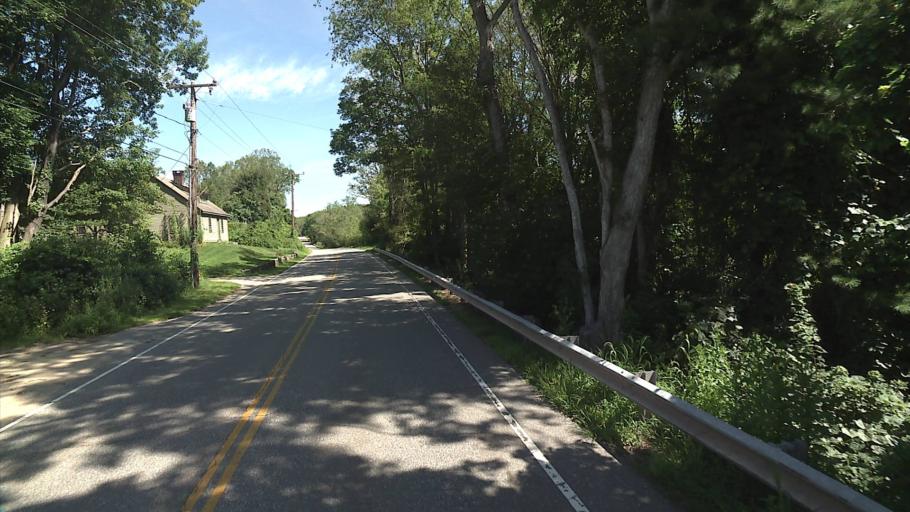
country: US
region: Connecticut
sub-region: New London County
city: Baltic
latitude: 41.6740
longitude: -72.0851
